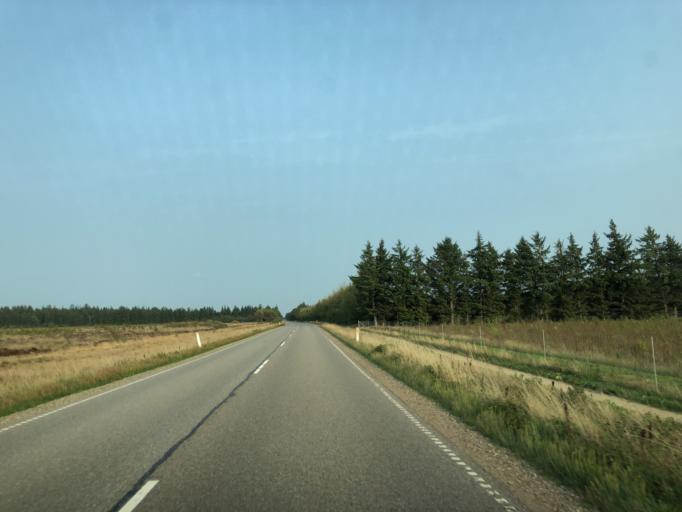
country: DK
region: South Denmark
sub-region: Billund Kommune
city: Grindsted
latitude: 55.8309
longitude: 8.9560
